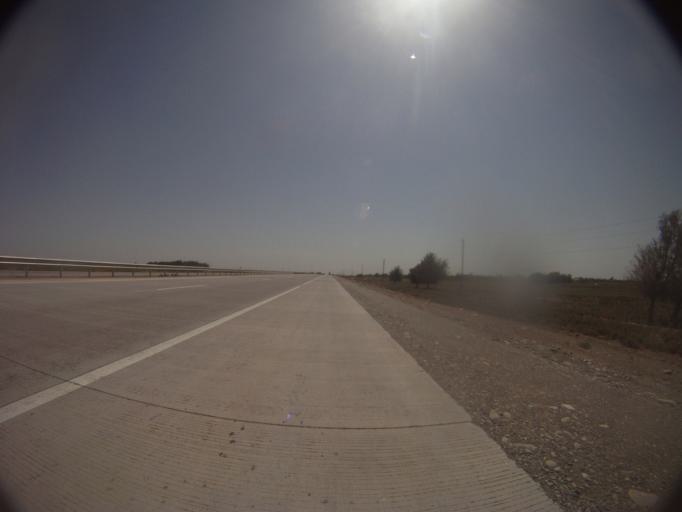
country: KZ
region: Ongtustik Qazaqstan
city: Bayaldyr
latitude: 43.0670
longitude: 68.6726
